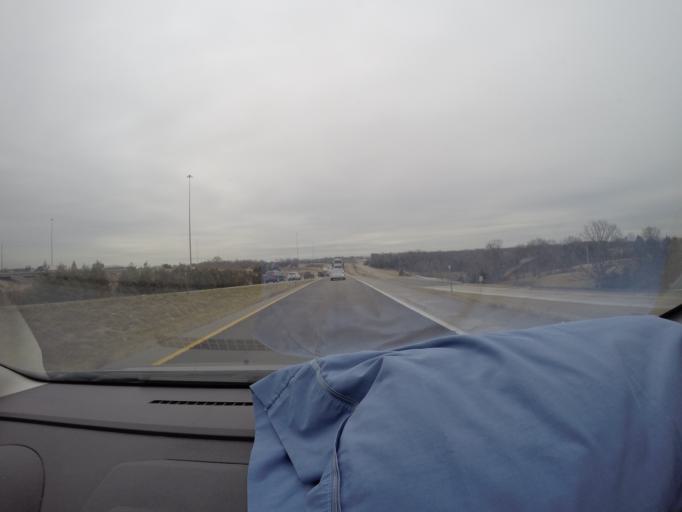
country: US
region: Missouri
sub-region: Saint Charles County
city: Wentzville
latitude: 38.8054
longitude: -90.8383
